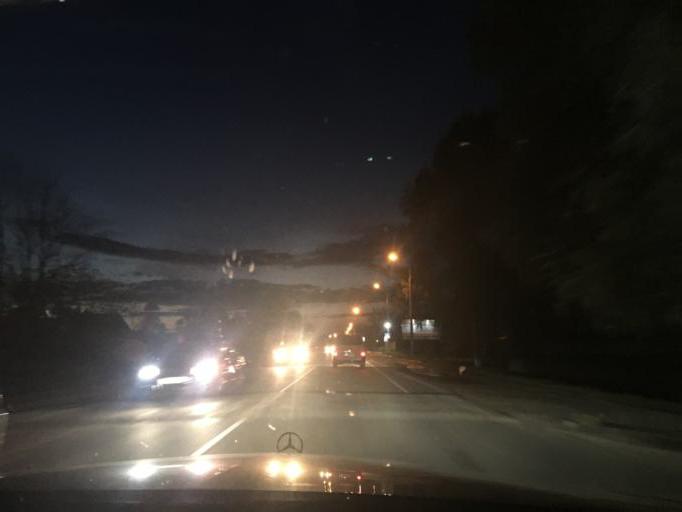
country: BY
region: Brest
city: Brest
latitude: 52.0556
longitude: 23.7214
